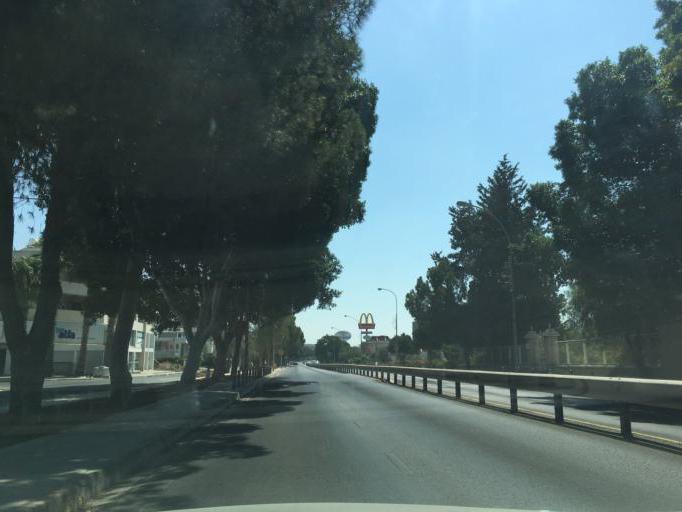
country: CY
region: Lefkosia
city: Nicosia
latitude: 35.1642
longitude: 33.3280
